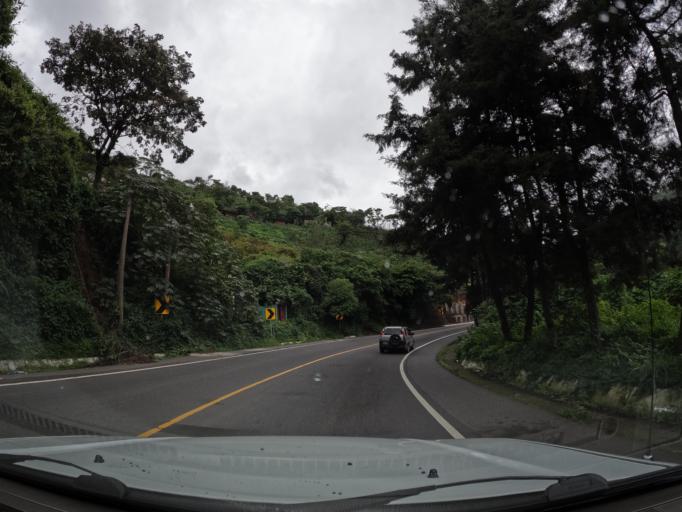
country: GT
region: Sacatepequez
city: Pastores
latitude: 14.6079
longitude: -90.7656
